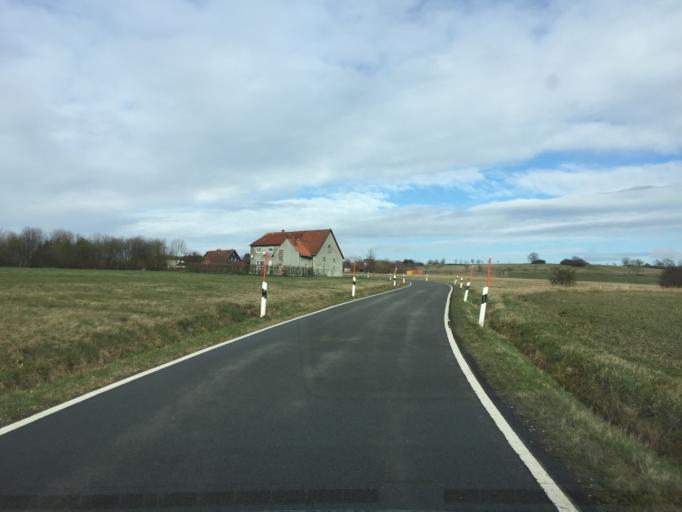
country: DE
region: Lower Saxony
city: Aerzen
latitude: 52.1008
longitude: 9.1595
